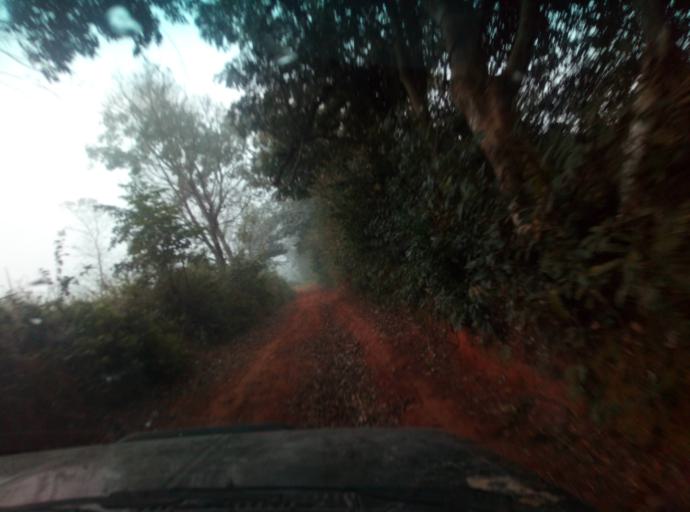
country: PY
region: Caaguazu
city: Doctor Cecilio Baez
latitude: -25.1514
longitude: -56.2518
